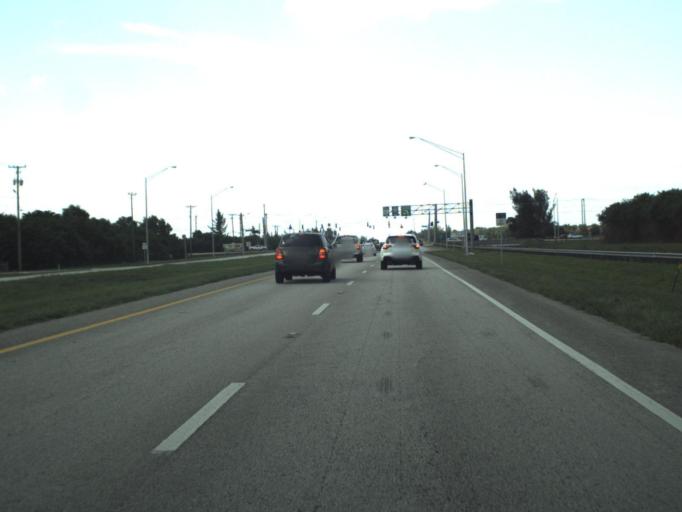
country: US
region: Florida
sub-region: Palm Beach County
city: Villages of Oriole
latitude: 26.4510
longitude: -80.2044
